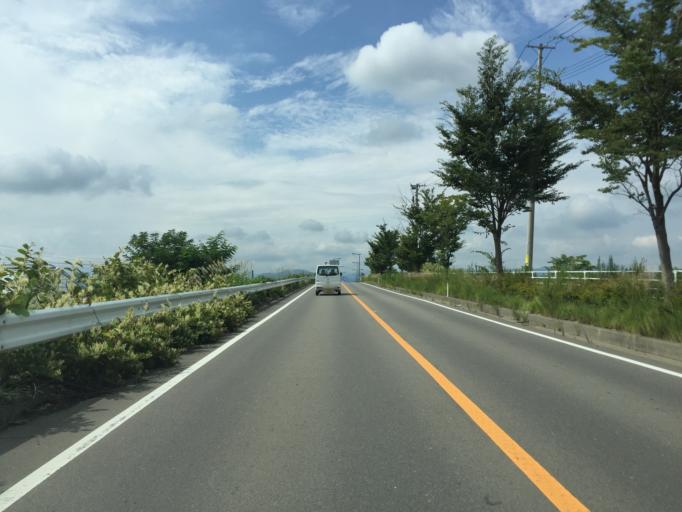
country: JP
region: Fukushima
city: Hobaramachi
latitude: 37.7971
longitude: 140.5094
